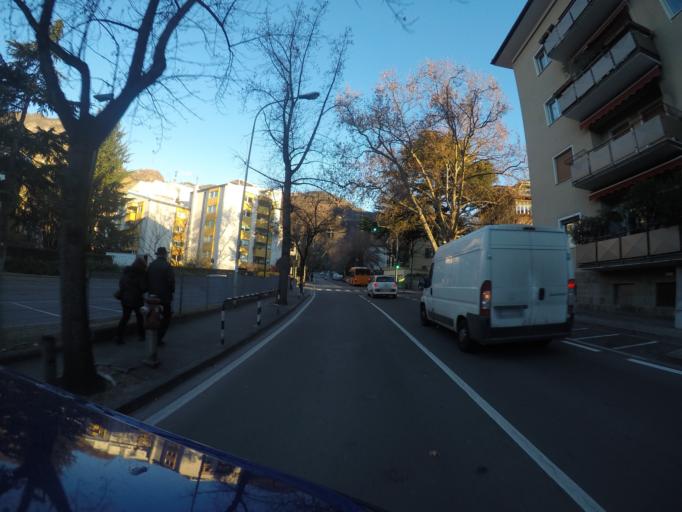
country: IT
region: Trentino-Alto Adige
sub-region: Bolzano
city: Bolzano
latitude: 46.5068
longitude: 11.3472
